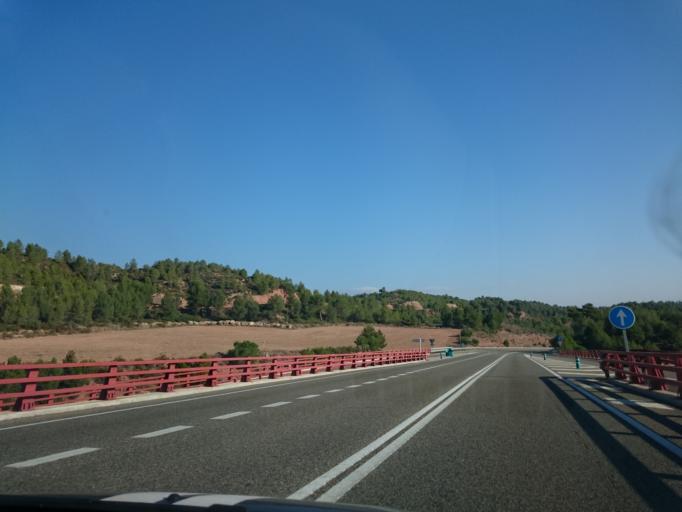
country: ES
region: Catalonia
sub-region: Provincia de Barcelona
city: Castellfollit del Boix
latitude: 41.6584
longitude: 1.7223
